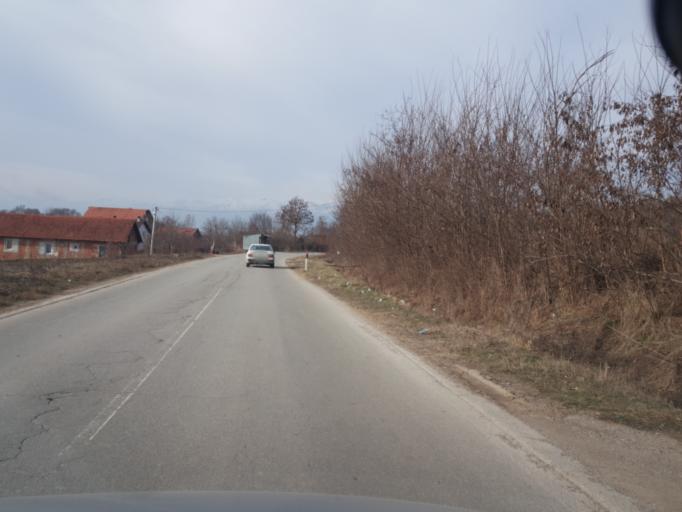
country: XK
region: Pec
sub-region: Komuna e Klines
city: Klina
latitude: 42.6687
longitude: 20.5359
